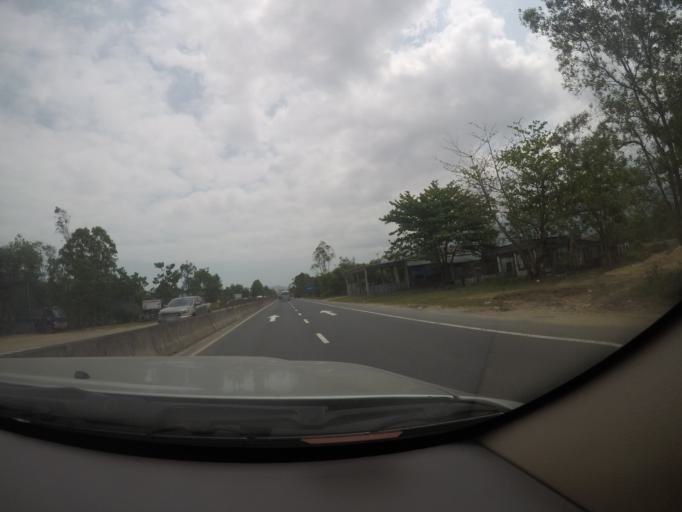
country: VN
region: Thua Thien-Hue
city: Phu Loc
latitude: 16.2722
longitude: 107.9592
